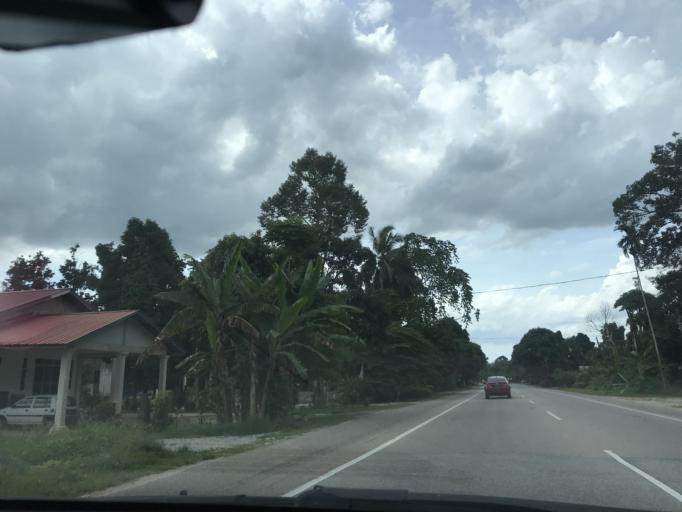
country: MY
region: Kelantan
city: Kampong Pangkal Kalong
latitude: 5.9340
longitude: 102.1915
